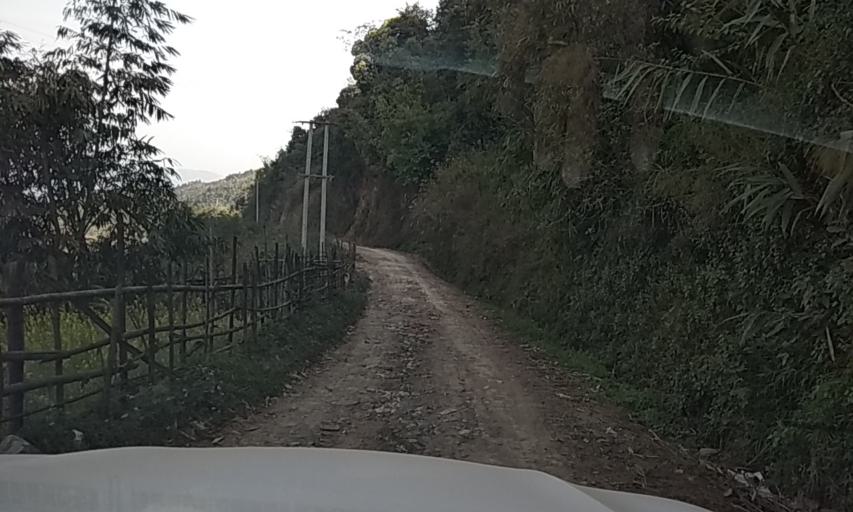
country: LA
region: Phongsali
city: Phongsali
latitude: 21.6840
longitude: 102.1006
